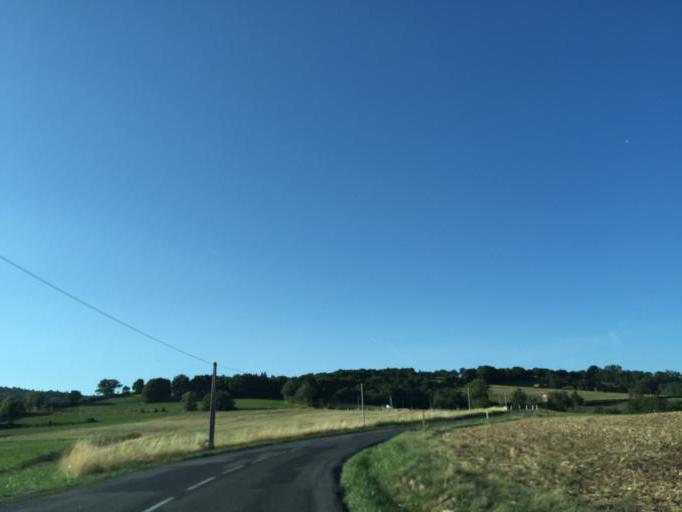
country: FR
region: Midi-Pyrenees
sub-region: Departement de l'Aveyron
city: Saint-Georges-de-Luzencon
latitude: 44.1103
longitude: 2.9034
